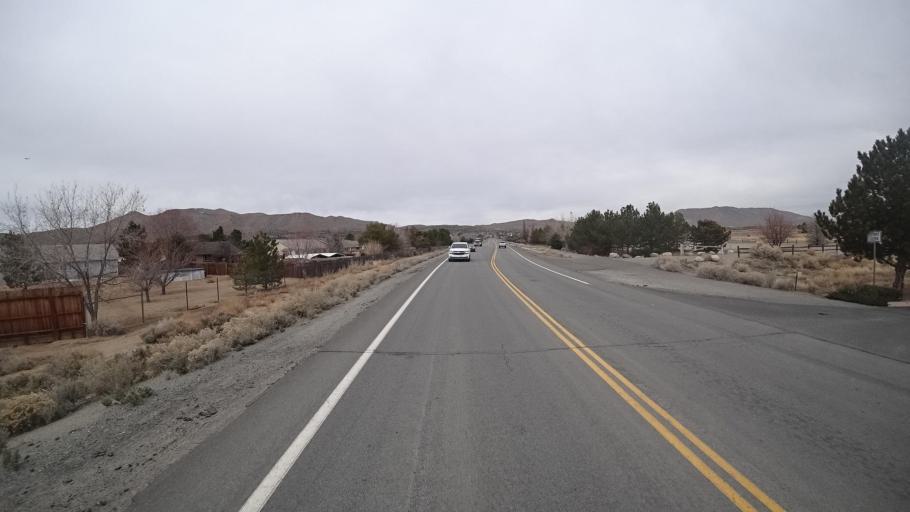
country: US
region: Nevada
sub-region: Washoe County
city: Spanish Springs
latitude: 39.6430
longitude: -119.7206
